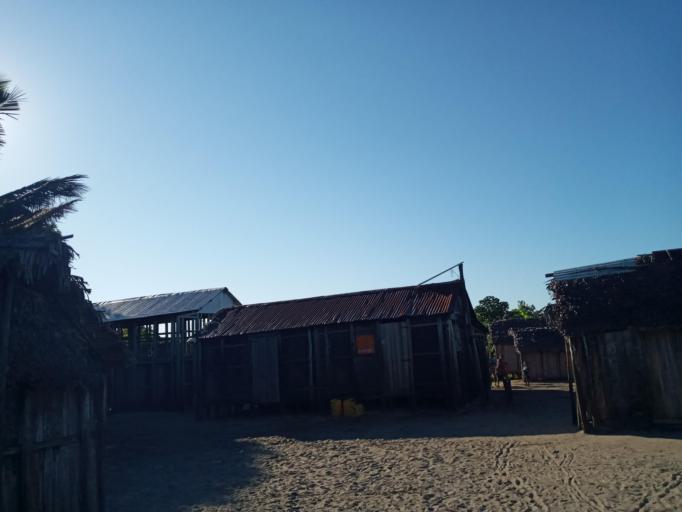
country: MG
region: Anosy
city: Fort Dauphin
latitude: -24.5969
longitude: 47.2396
